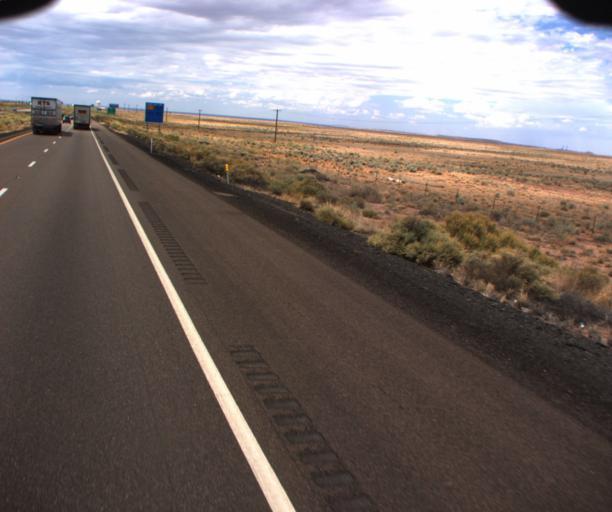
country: US
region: Arizona
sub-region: Navajo County
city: Holbrook
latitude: 34.9499
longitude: -110.1184
